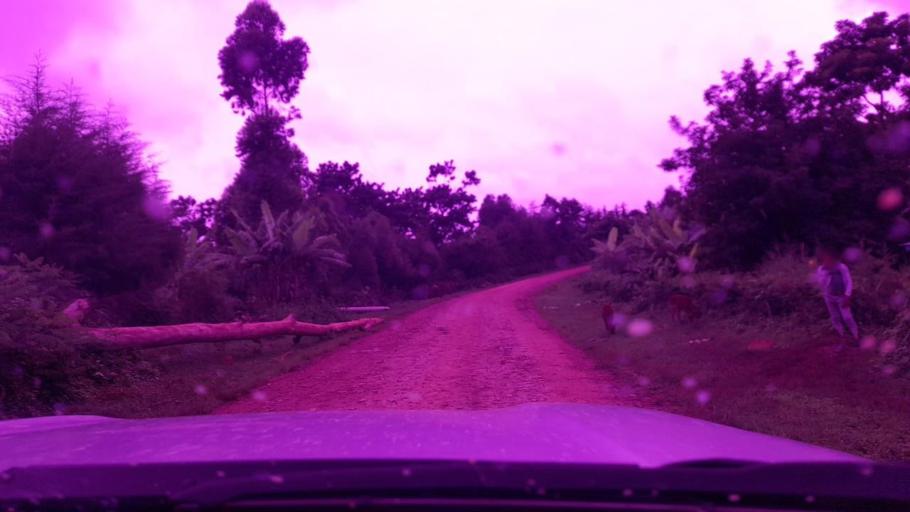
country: ET
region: Southern Nations, Nationalities, and People's Region
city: Bonga
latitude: 7.5495
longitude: 35.8653
